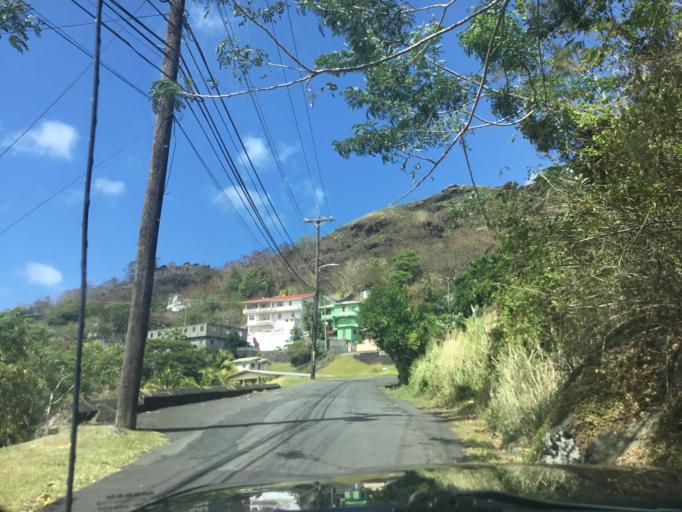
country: VC
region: Saint George
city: Kingstown Park
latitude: 13.1611
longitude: -61.2345
